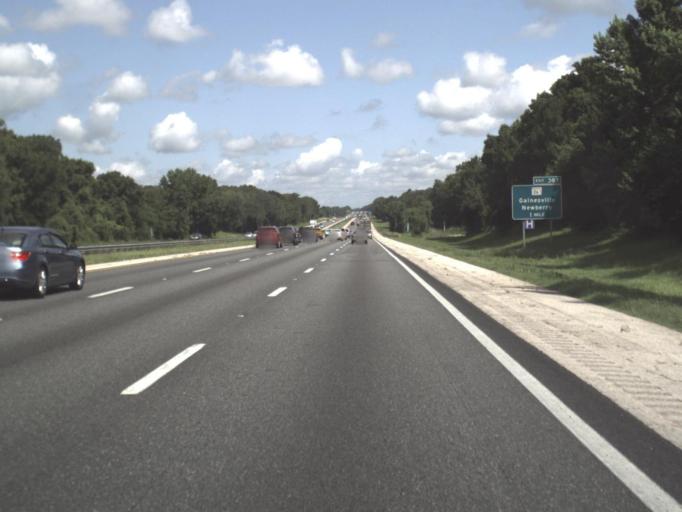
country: US
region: Florida
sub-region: Alachua County
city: Gainesville
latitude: 29.6432
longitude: -82.4047
